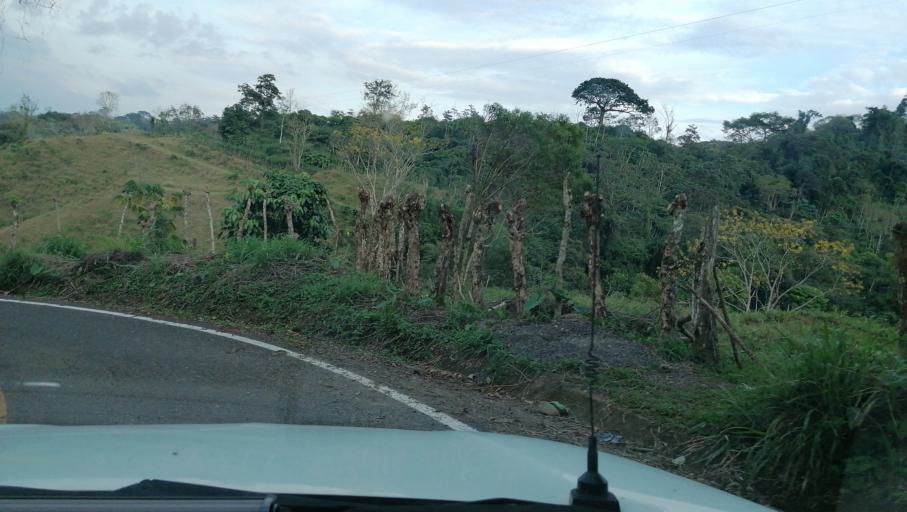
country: MX
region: Chiapas
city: Pichucalco
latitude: 17.5135
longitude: -93.2057
